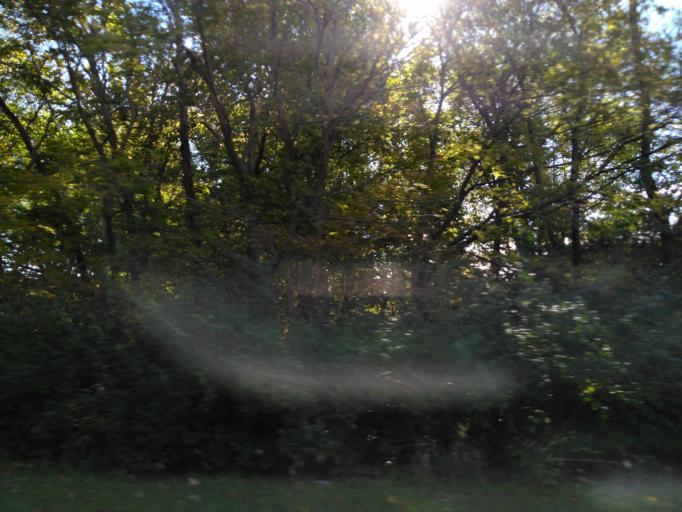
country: US
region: Illinois
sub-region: Madison County
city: Highland
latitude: 38.7642
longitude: -89.6560
